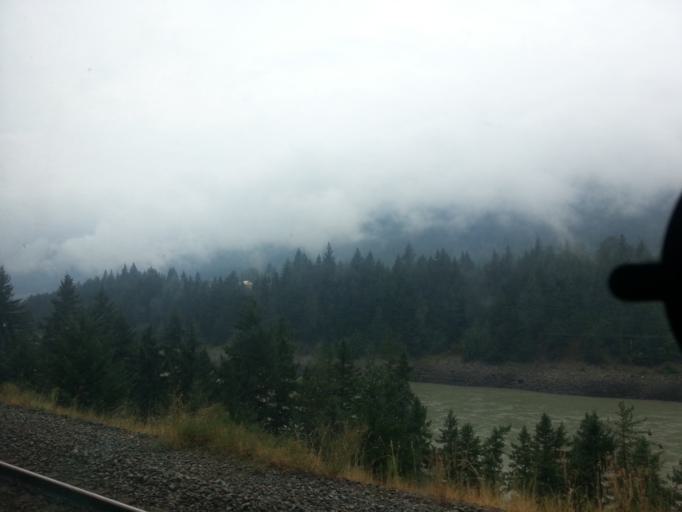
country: CA
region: British Columbia
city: Hope
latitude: 49.8845
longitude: -121.4431
